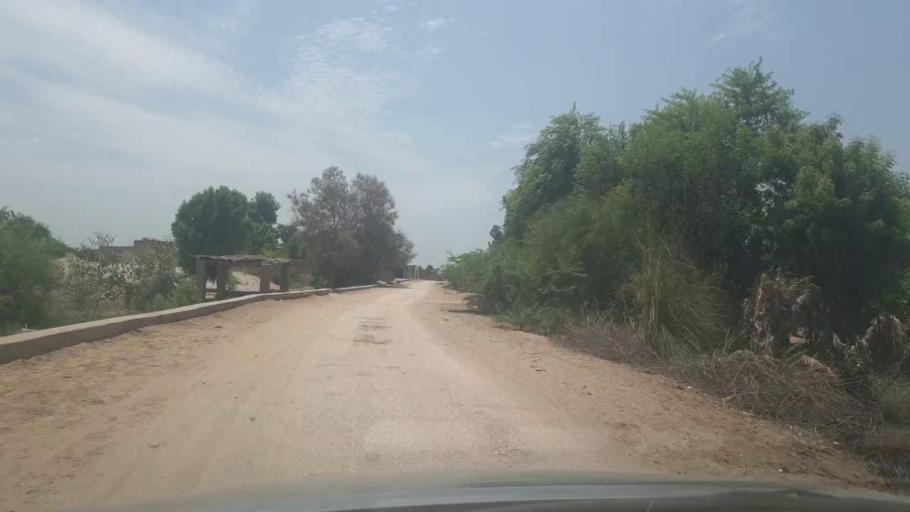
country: PK
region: Sindh
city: Kot Diji
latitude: 27.4112
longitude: 68.7353
